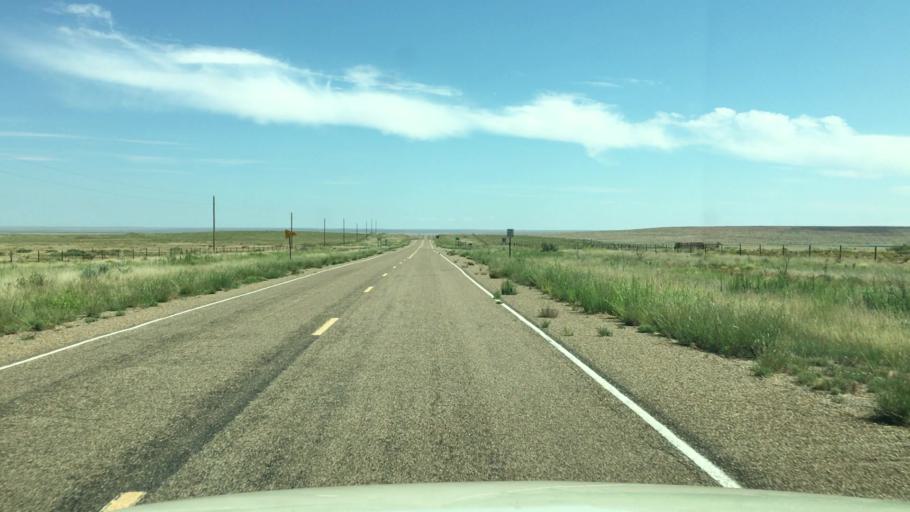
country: US
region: New Mexico
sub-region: De Baca County
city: Fort Sumner
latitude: 33.9956
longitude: -104.5682
